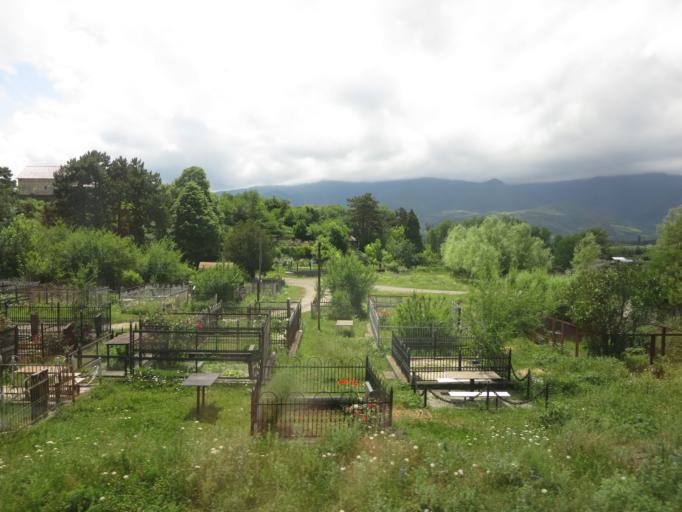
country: GE
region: Shida Kartli
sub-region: Khashuris Raioni
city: Khashuri
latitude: 41.9952
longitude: 43.5804
